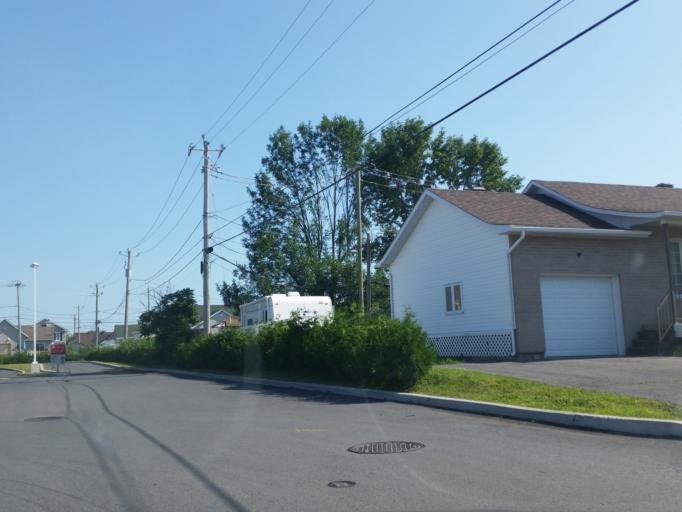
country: CA
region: Quebec
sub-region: Monteregie
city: Saint-Jean-sur-Richelieu
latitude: 45.2748
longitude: -73.2738
